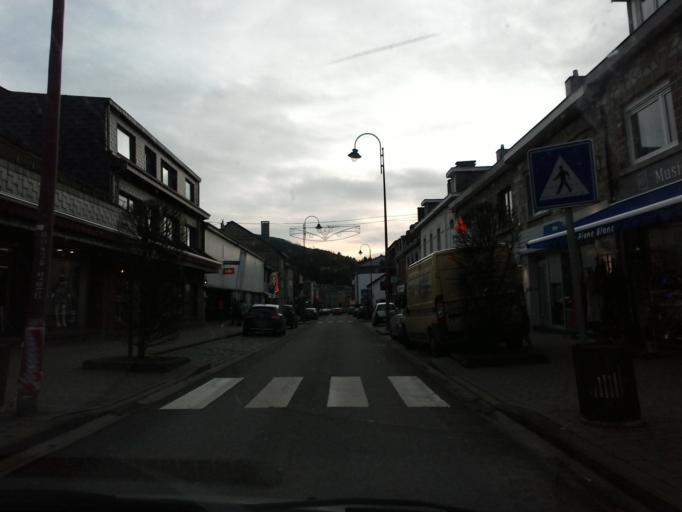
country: BE
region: Wallonia
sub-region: Province du Luxembourg
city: Vielsalm
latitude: 50.2863
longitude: 5.9152
